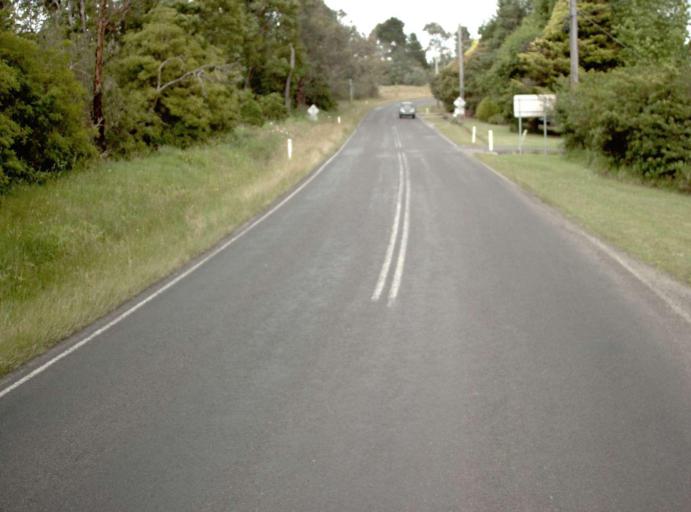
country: AU
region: Victoria
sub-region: Baw Baw
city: Warragul
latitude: -38.0907
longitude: 145.8528
